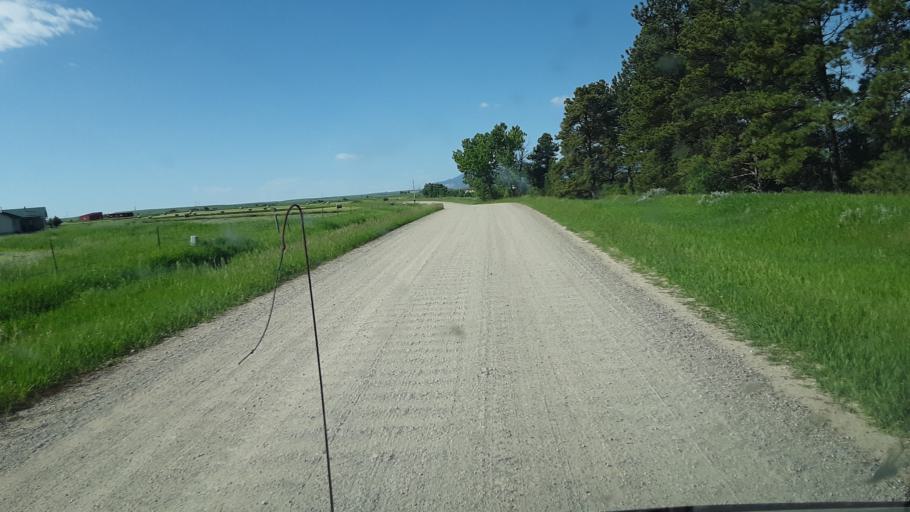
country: US
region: Montana
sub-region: Carbon County
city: Red Lodge
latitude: 45.3552
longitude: -109.1593
